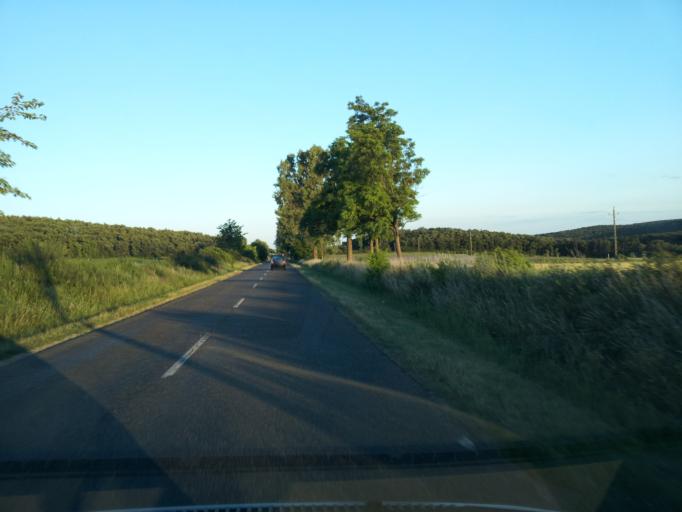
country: HU
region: Veszprem
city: Szentkiralyszabadja
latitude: 47.0239
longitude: 17.9416
